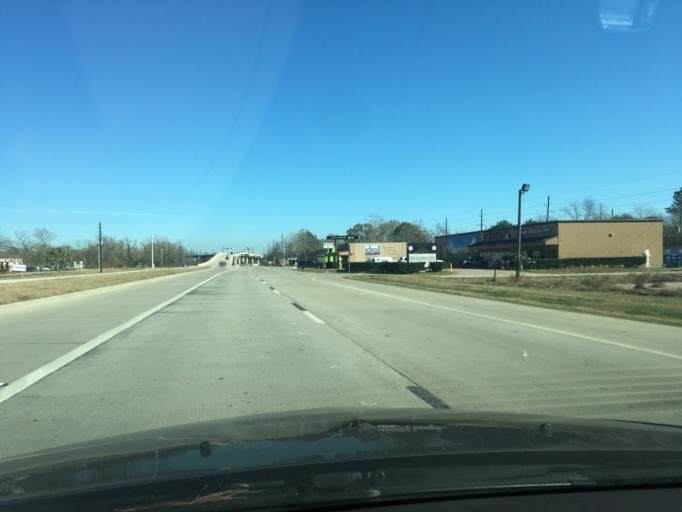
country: US
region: Texas
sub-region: Fort Bend County
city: Richmond
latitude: 29.5903
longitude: -95.7469
